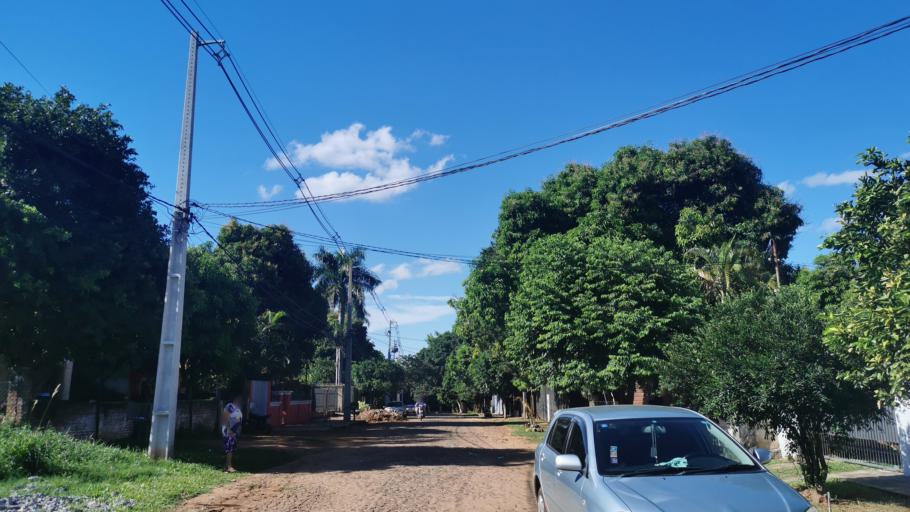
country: PY
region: Central
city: San Lorenzo
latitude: -25.3280
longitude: -57.5081
